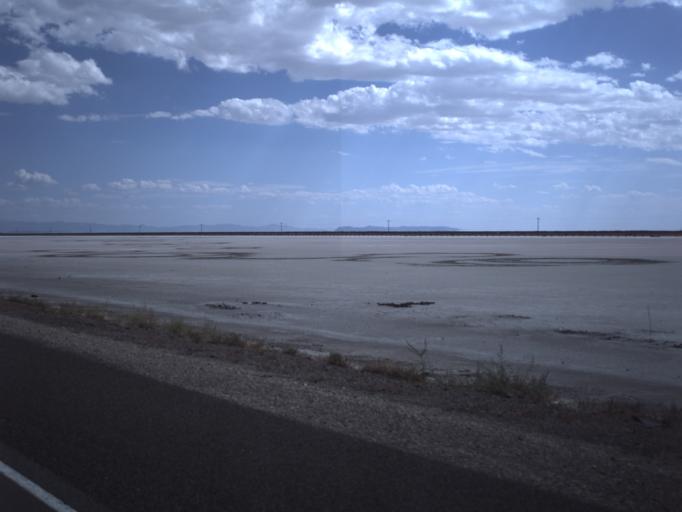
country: US
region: Utah
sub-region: Tooele County
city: Wendover
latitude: 40.7350
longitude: -113.6821
